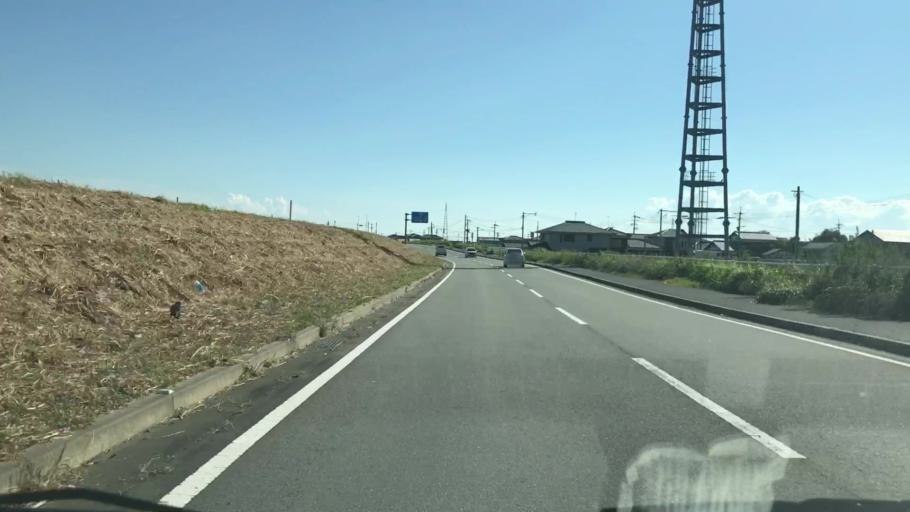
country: JP
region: Saga Prefecture
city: Okawa
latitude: 33.2390
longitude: 130.3812
